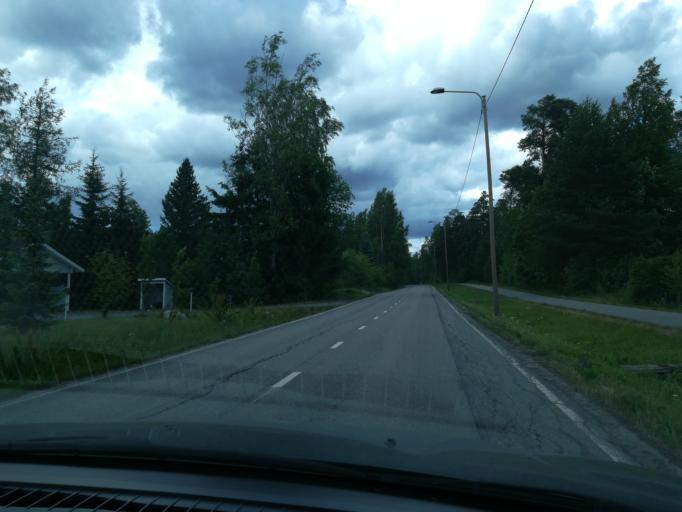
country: FI
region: Southern Savonia
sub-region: Mikkeli
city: Hirvensalmi
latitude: 61.6498
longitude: 26.7713
